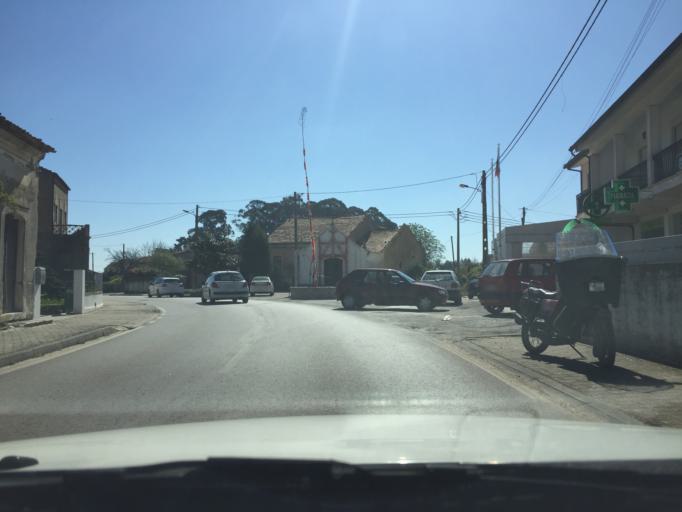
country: PT
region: Aveiro
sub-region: Anadia
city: Sangalhos
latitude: 40.4202
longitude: -8.5283
